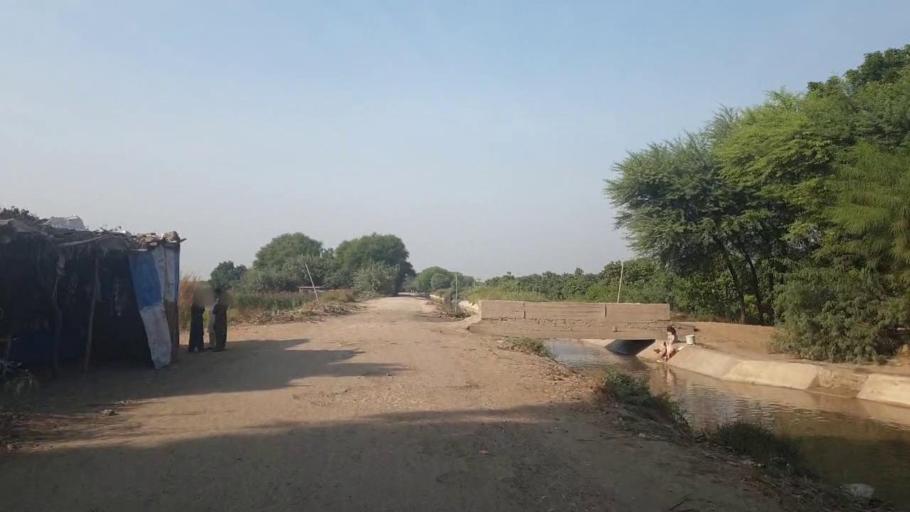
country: PK
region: Sindh
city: Tando Jam
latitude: 25.4127
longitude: 68.4653
